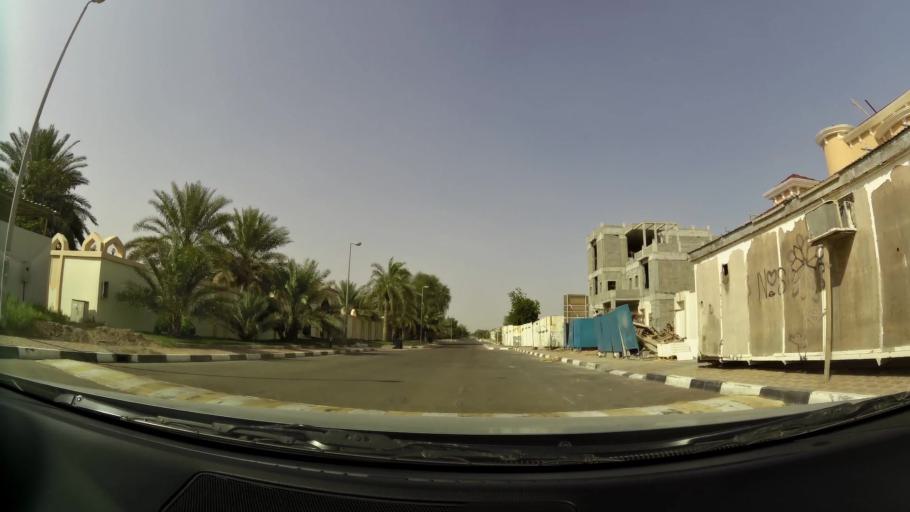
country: AE
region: Abu Dhabi
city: Al Ain
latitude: 24.2478
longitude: 55.6837
